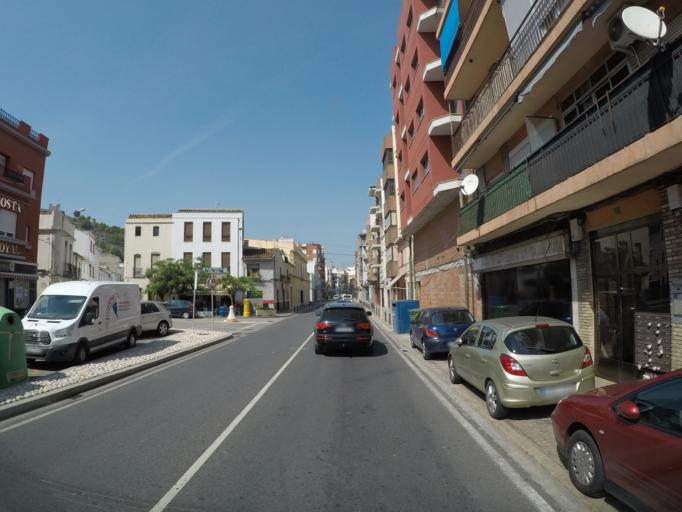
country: ES
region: Valencia
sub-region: Provincia de Valencia
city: Oliva
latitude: 38.9165
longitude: -0.1160
